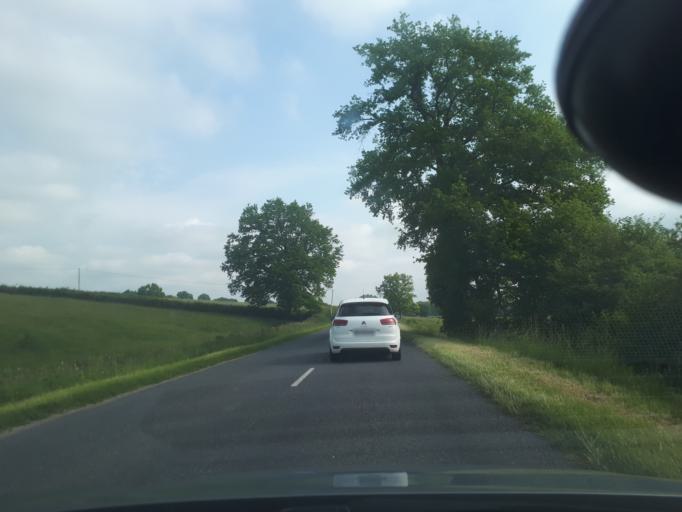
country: FR
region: Auvergne
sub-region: Departement de l'Allier
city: Saint-Gerand-le-Puy
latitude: 46.3664
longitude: 3.5797
